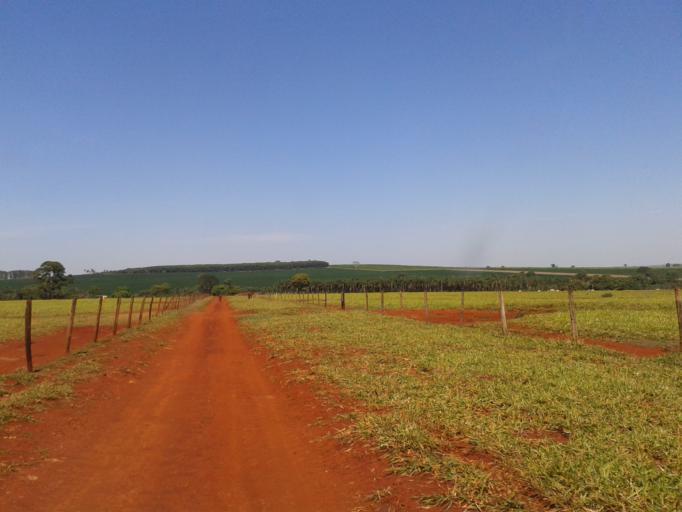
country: BR
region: Minas Gerais
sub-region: Centralina
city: Centralina
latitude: -18.6521
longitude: -49.2897
